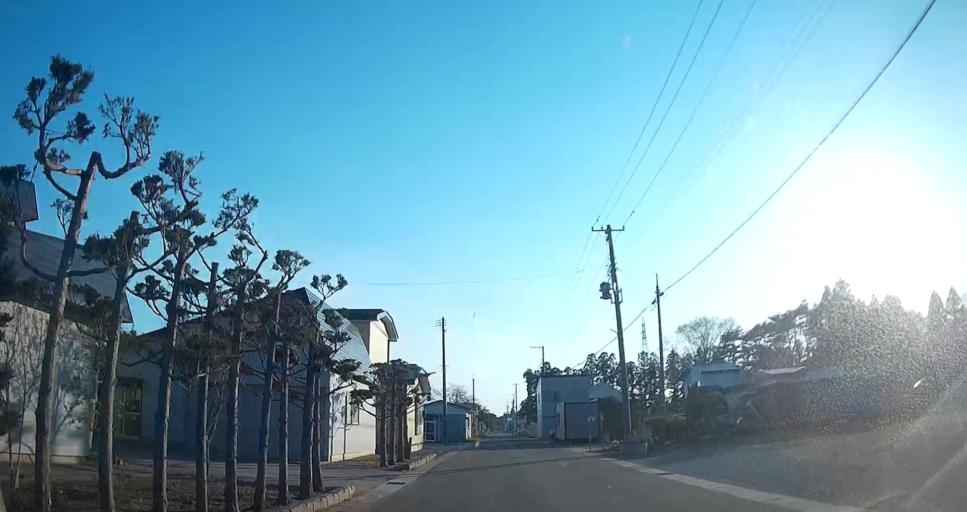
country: JP
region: Aomori
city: Mutsu
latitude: 41.2660
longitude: 141.2204
